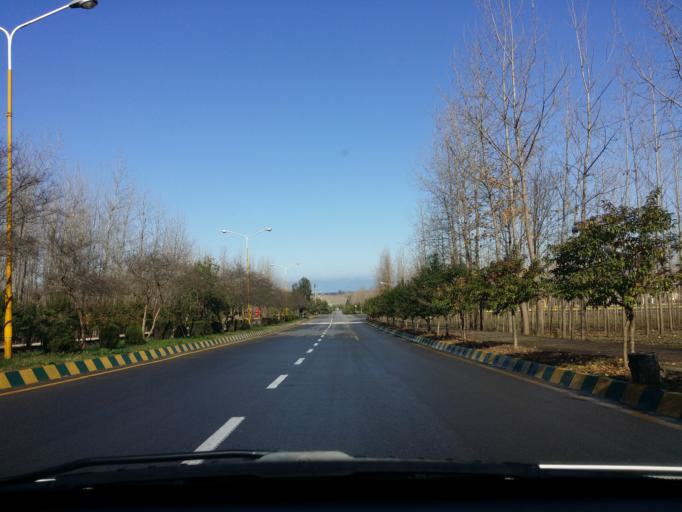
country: IR
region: Mazandaran
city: Chalus
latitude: 36.6664
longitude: 51.3074
